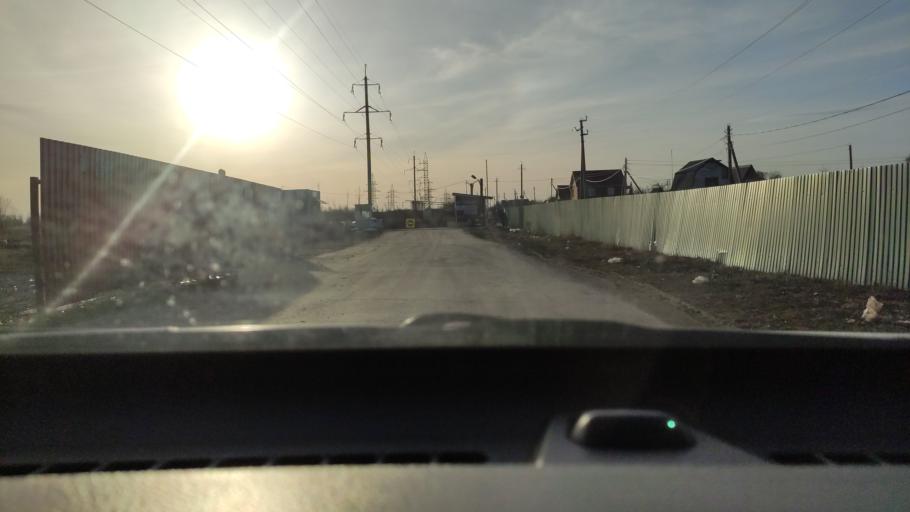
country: RU
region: Samara
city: Podstepki
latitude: 53.5941
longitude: 49.2195
